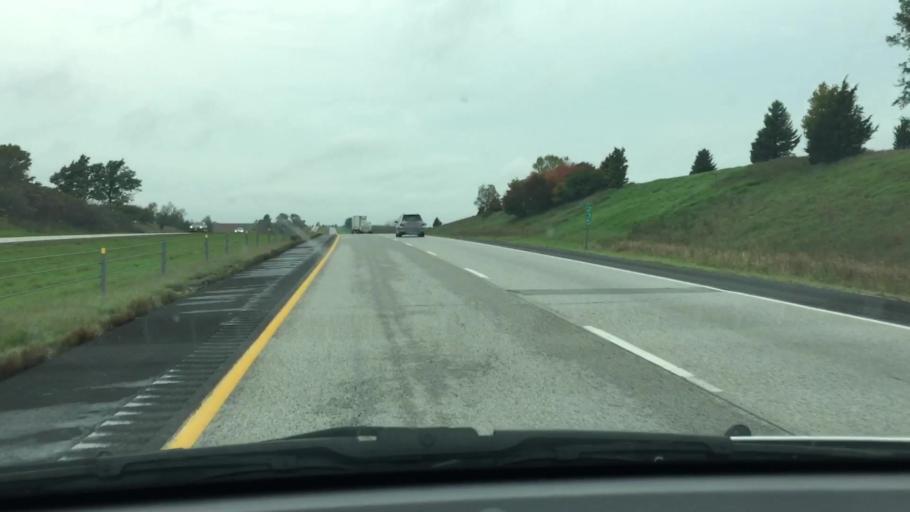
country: US
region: Iowa
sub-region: Johnson County
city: Tiffin
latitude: 41.6954
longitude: -91.7175
